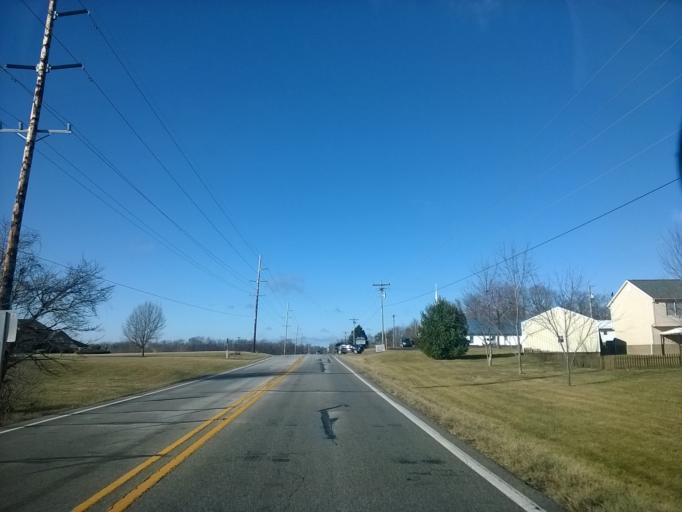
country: US
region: Indiana
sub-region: Scott County
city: Scottsburg
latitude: 38.7367
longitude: -85.6916
